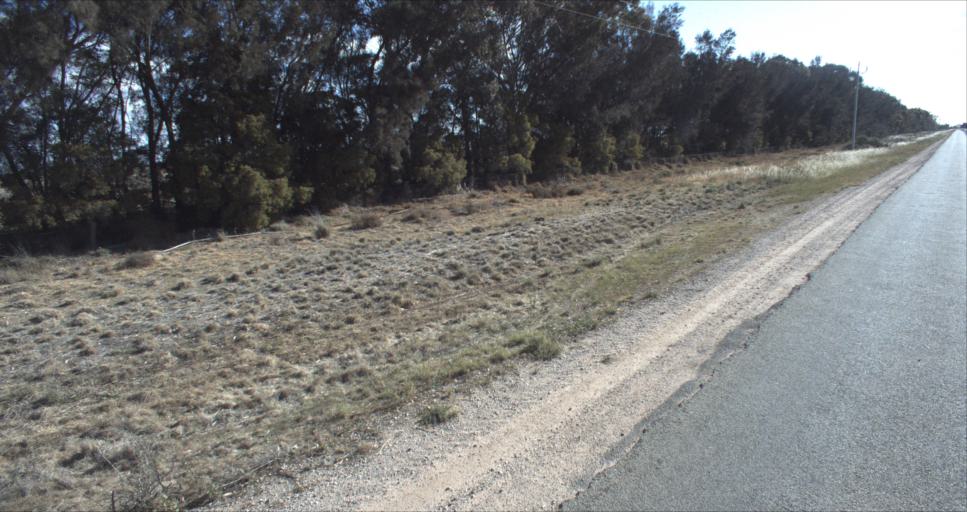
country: AU
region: New South Wales
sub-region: Leeton
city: Leeton
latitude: -34.4583
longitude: 146.2695
